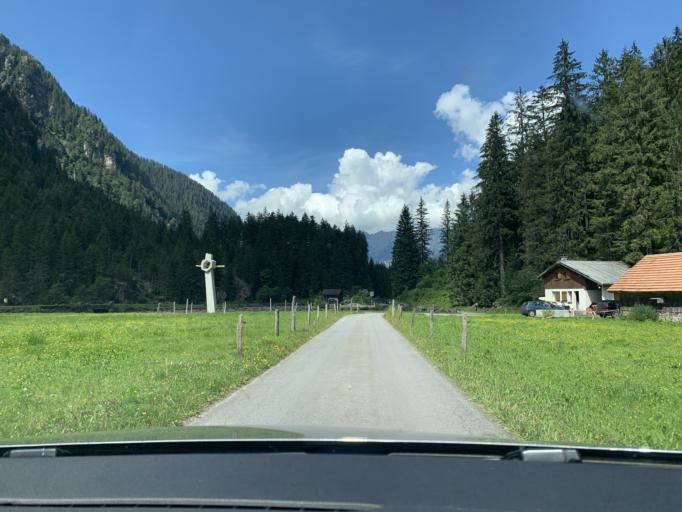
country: CH
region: Saint Gallen
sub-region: Wahlkreis Sarganserland
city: Quarten
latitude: 47.0751
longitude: 9.1982
